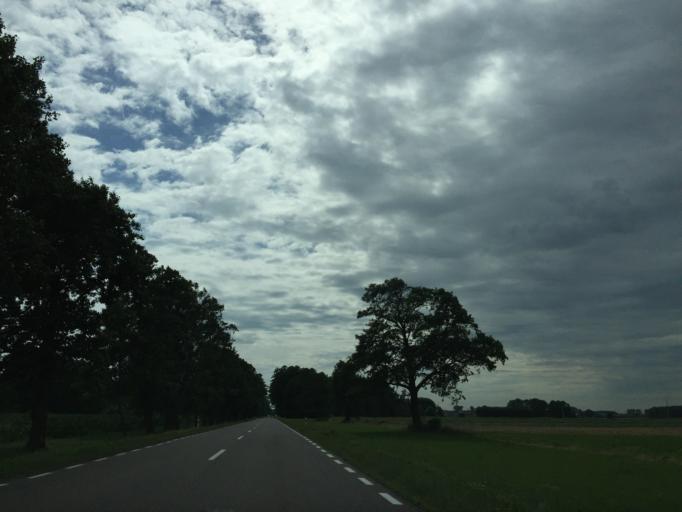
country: PL
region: Podlasie
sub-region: Powiat bielski
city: Bocki
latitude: 52.6318
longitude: 23.0168
